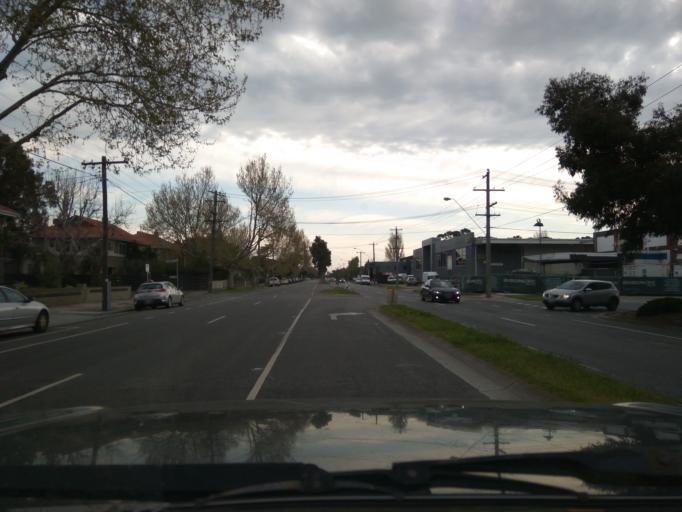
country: AU
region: Victoria
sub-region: Port Phillip
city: Port Melbourne
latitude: -37.8350
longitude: 144.9255
